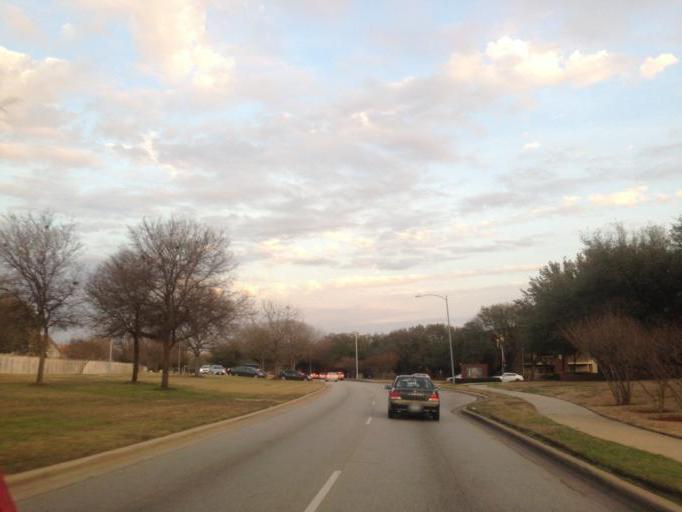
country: US
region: Texas
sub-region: Travis County
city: Wells Branch
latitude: 30.4351
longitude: -97.6816
